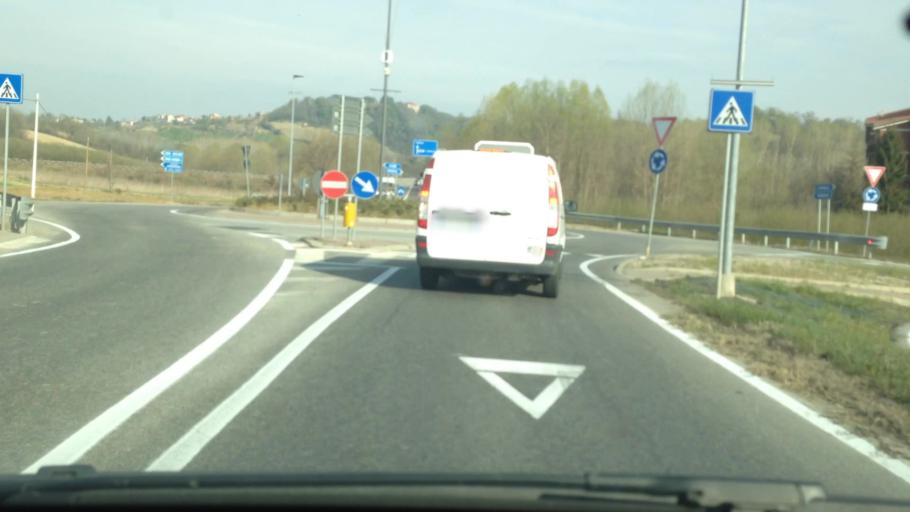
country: IT
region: Piedmont
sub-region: Provincia di Cuneo
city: Canale
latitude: 44.8002
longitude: 7.9802
